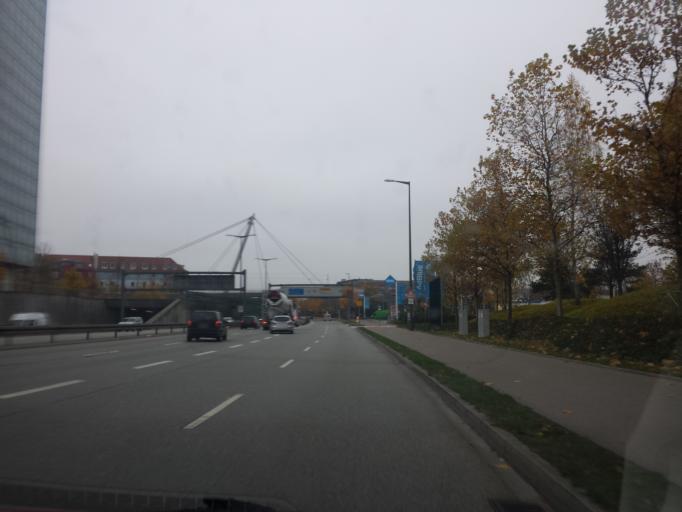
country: DE
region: Bavaria
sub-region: Upper Bavaria
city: Bogenhausen
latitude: 48.1765
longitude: 11.5911
